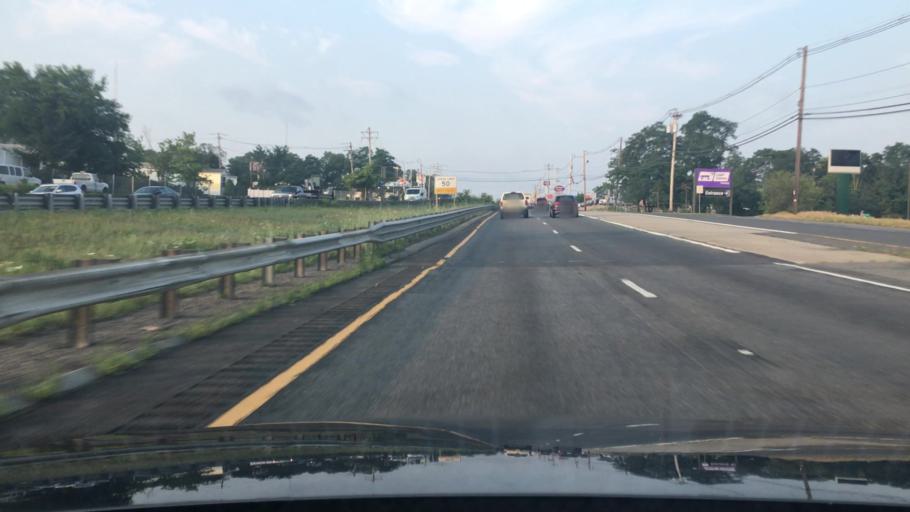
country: US
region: Massachusetts
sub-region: Essex County
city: South Peabody
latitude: 42.5408
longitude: -70.9868
